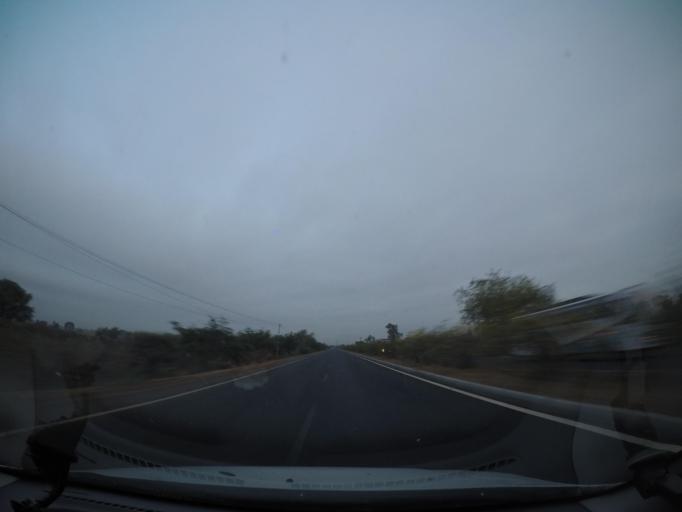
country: IN
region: Andhra Pradesh
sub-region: West Godavari
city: Tadepallegudem
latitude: 16.8100
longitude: 81.3361
